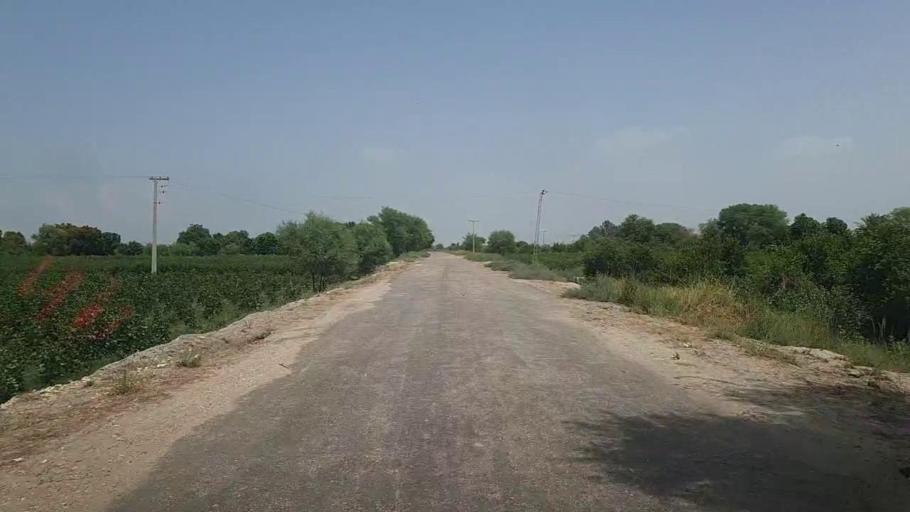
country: PK
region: Sindh
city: Pad Idan
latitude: 26.8445
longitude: 68.3261
